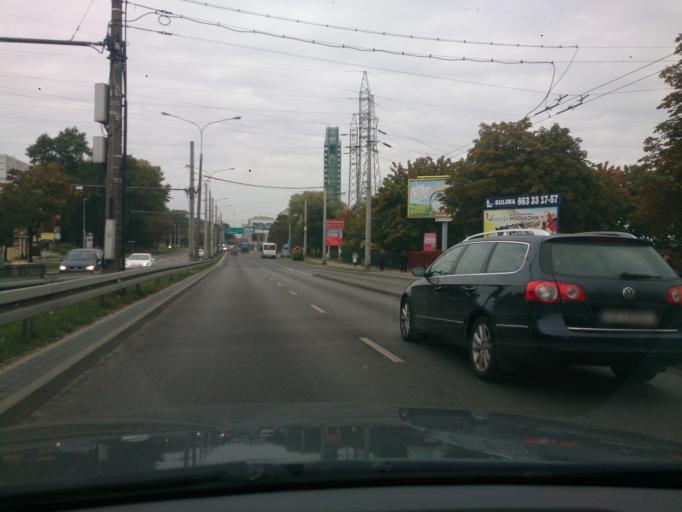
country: PL
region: Pomeranian Voivodeship
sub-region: Gdynia
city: Pogorze
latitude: 54.5316
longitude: 18.4947
